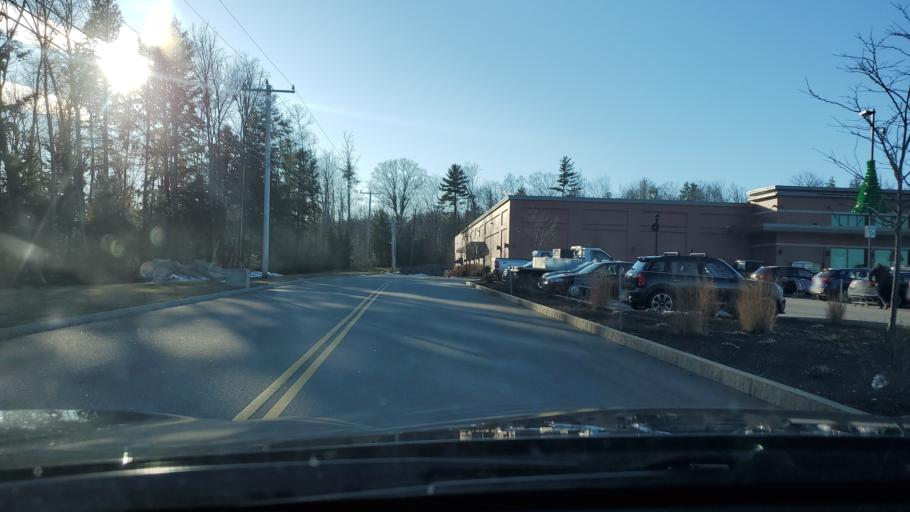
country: US
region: New Hampshire
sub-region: Strafford County
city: Rochester
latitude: 43.3306
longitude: -71.0088
